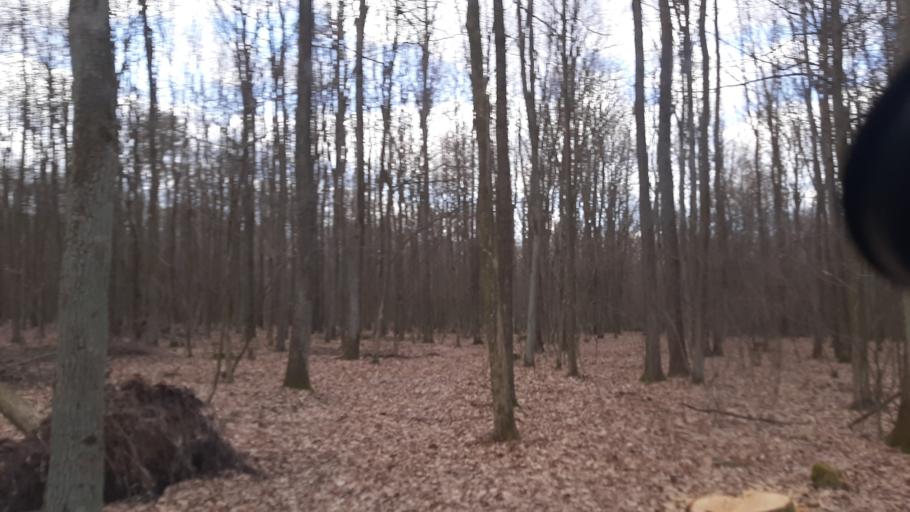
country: PL
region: Lublin Voivodeship
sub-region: Powiat lubelski
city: Jastkow
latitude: 51.3735
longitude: 22.4128
